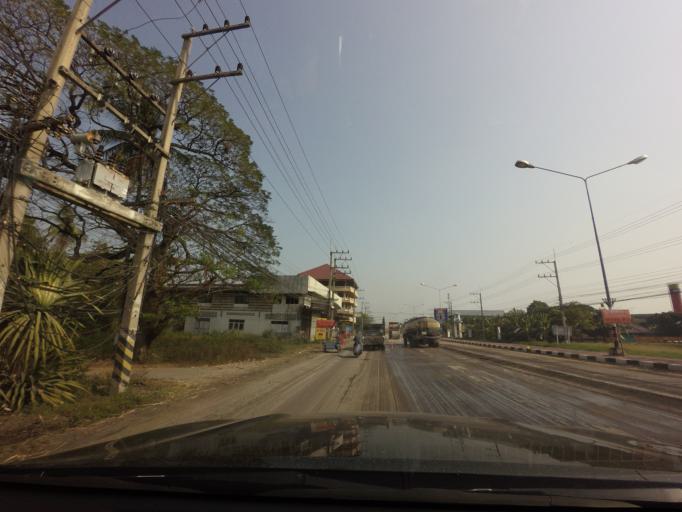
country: TH
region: Kanchanaburi
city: Tha Maka
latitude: 13.8950
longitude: 99.7959
